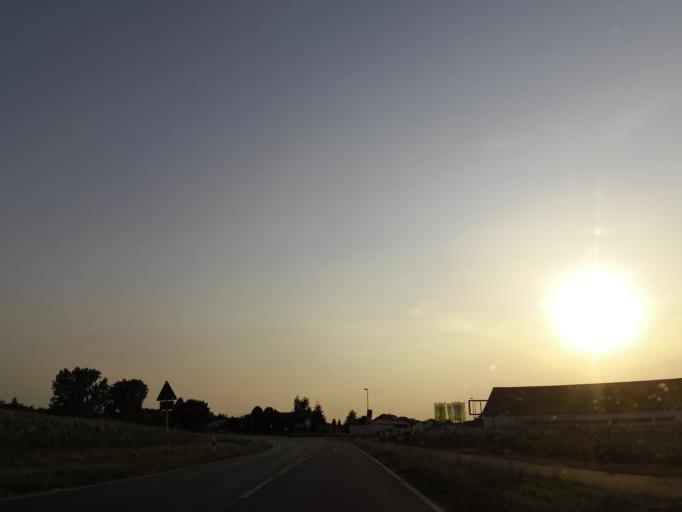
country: DE
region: Hesse
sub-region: Regierungsbezirk Darmstadt
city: Buttelborn
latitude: 49.9211
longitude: 8.5302
